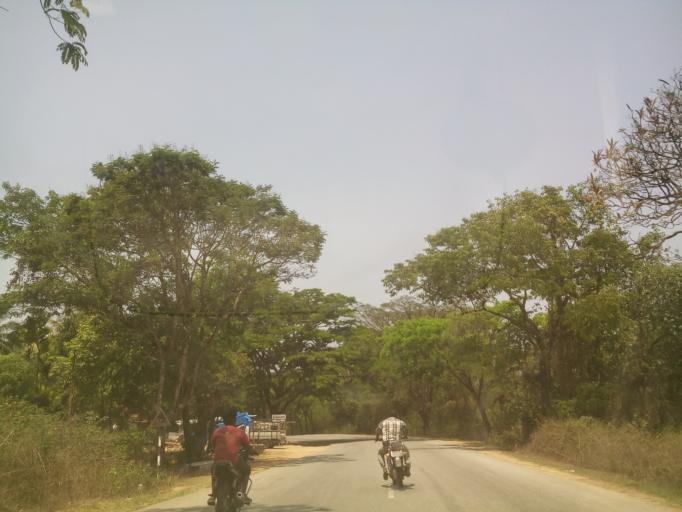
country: IN
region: Karnataka
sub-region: Hassan
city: Sakleshpur
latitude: 12.9541
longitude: 75.8584
